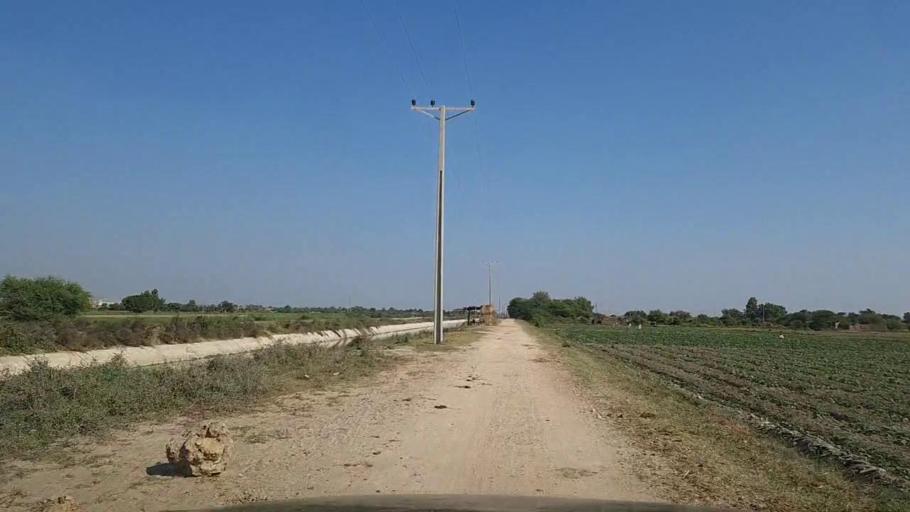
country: PK
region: Sindh
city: Mirpur Sakro
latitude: 24.5967
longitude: 67.8066
